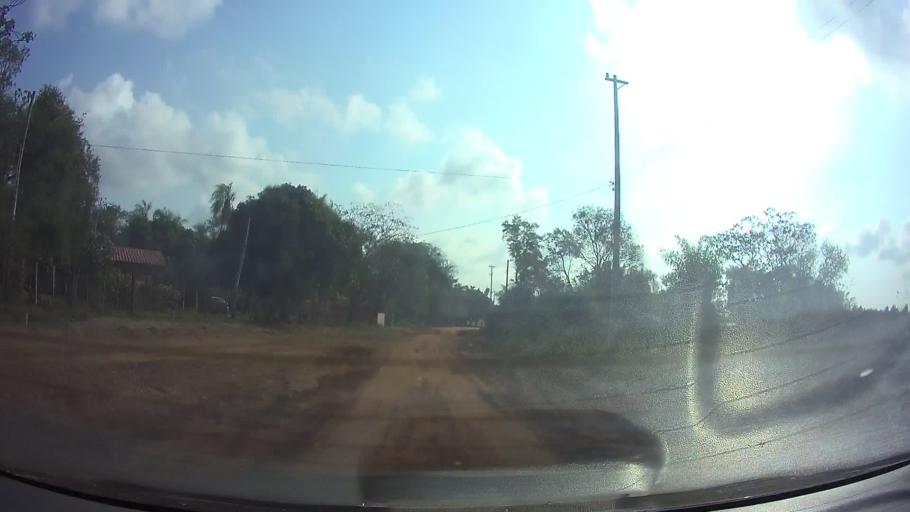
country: PY
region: Cordillera
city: Arroyos y Esteros
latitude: -25.0523
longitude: -57.1819
